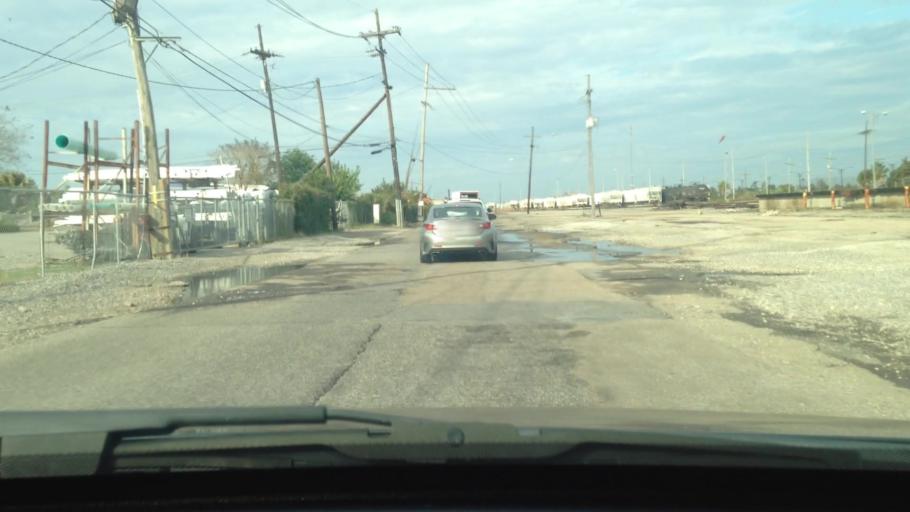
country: US
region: Louisiana
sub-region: Jefferson Parish
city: Jefferson
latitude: 29.9716
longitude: -90.1290
